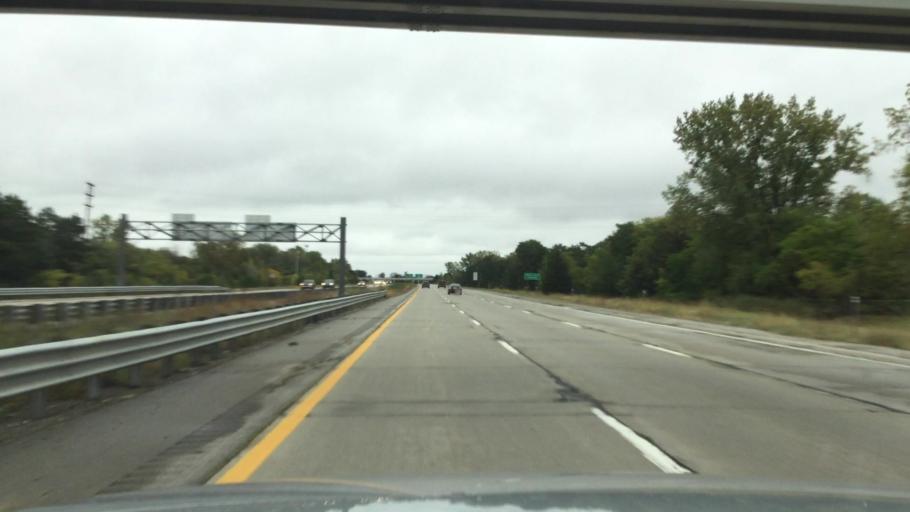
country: US
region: Michigan
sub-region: Saginaw County
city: Buena Vista
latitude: 43.4339
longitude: -83.9084
